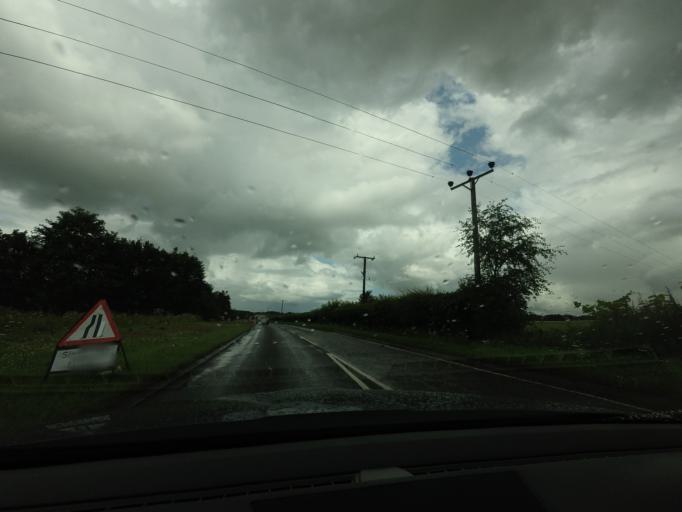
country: GB
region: Scotland
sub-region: Aberdeenshire
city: Turriff
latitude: 57.5495
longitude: -2.4424
